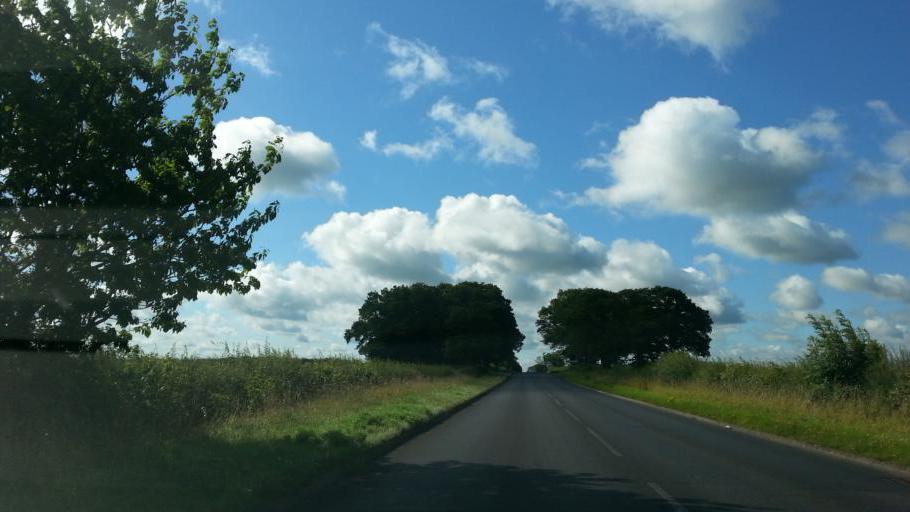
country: GB
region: England
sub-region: Staffordshire
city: Barton under Needwood
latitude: 52.8277
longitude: -1.7795
